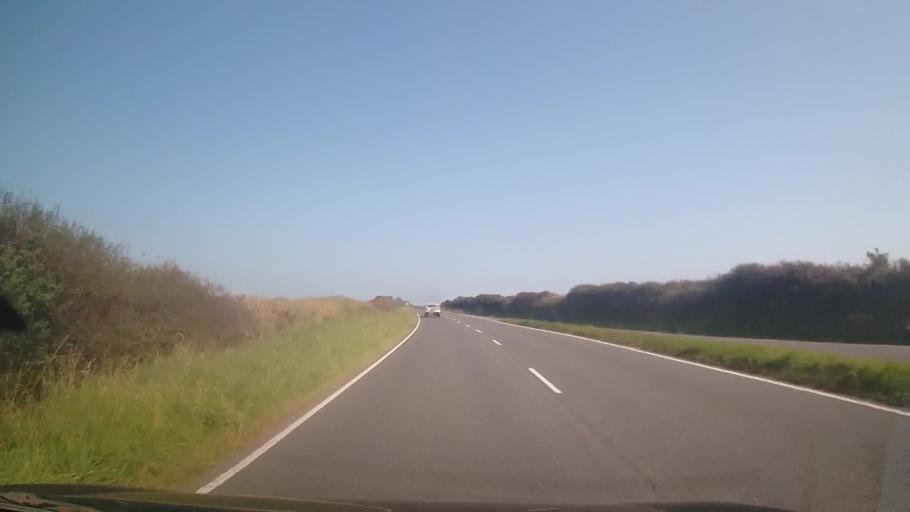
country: GB
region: Wales
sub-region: Pembrokeshire
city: Llanrhian
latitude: 51.9009
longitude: -5.2131
